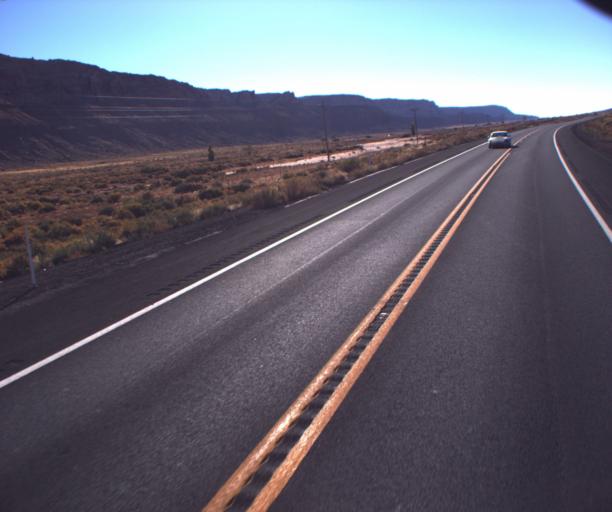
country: US
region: Arizona
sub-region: Coconino County
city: LeChee
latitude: 36.5076
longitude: -111.5846
